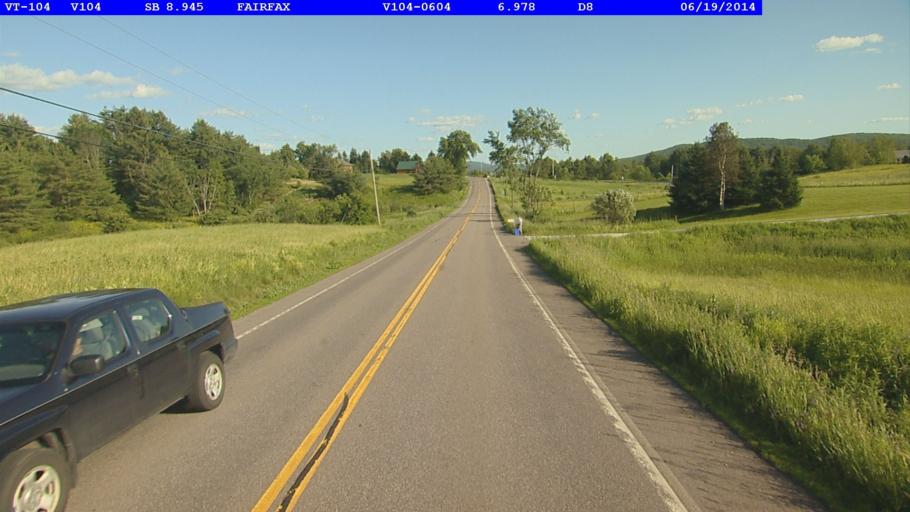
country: US
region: Vermont
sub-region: Chittenden County
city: Milton
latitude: 44.6859
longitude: -73.0307
